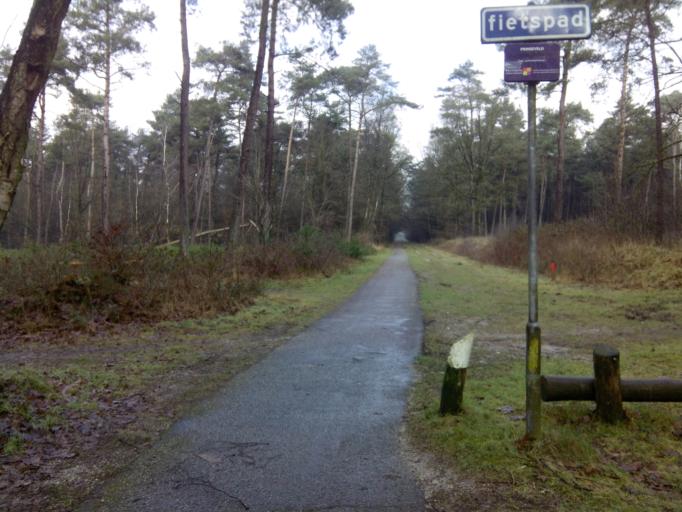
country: NL
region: Utrecht
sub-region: Gemeente Utrechtse Heuvelrug
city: Overberg
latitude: 52.0061
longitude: 5.5020
